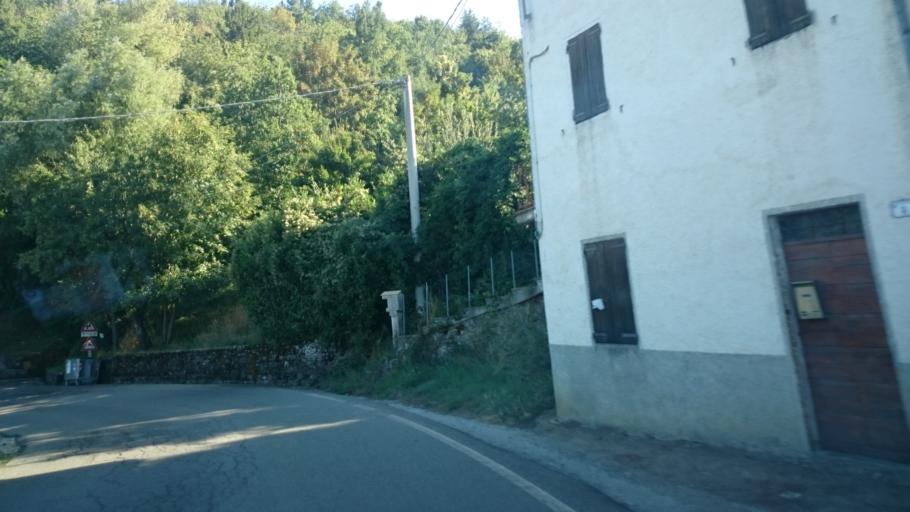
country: IT
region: Emilia-Romagna
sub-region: Provincia di Reggio Emilia
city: Villa Minozzo
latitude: 44.3488
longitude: 10.4929
